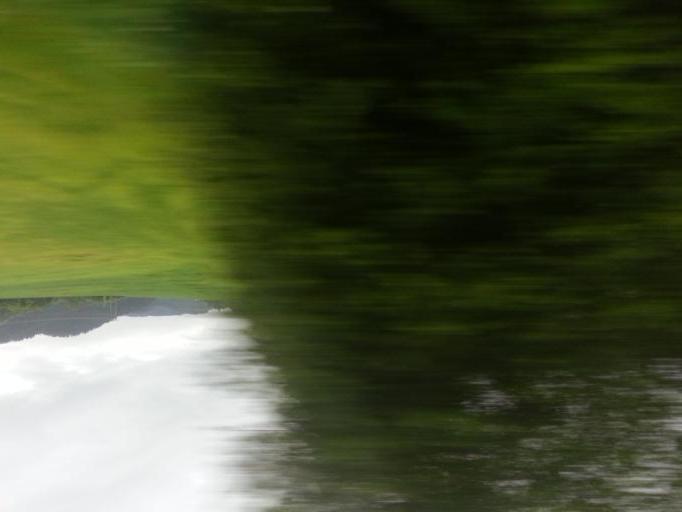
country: NO
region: Sor-Trondelag
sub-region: Melhus
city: Lundamo
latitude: 63.1569
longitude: 10.2854
